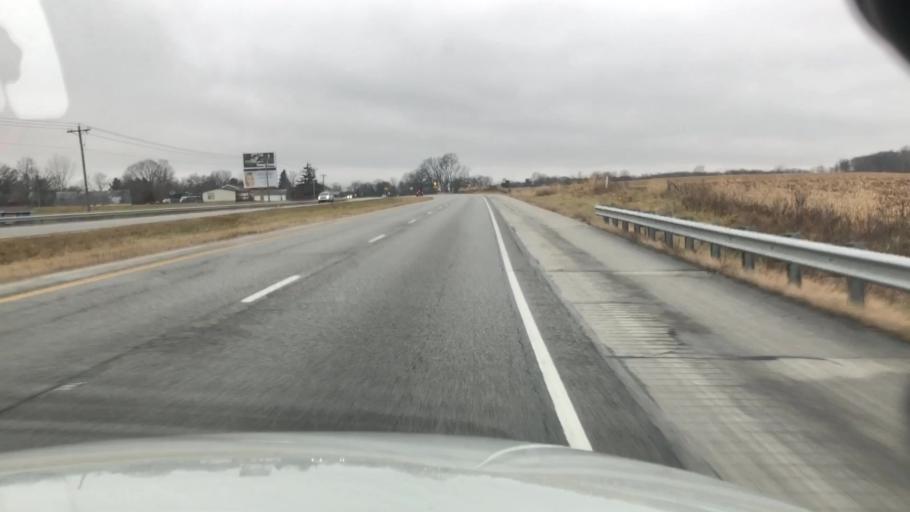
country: US
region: Indiana
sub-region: Kosciusko County
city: Pierceton
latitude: 41.1795
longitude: -85.6173
